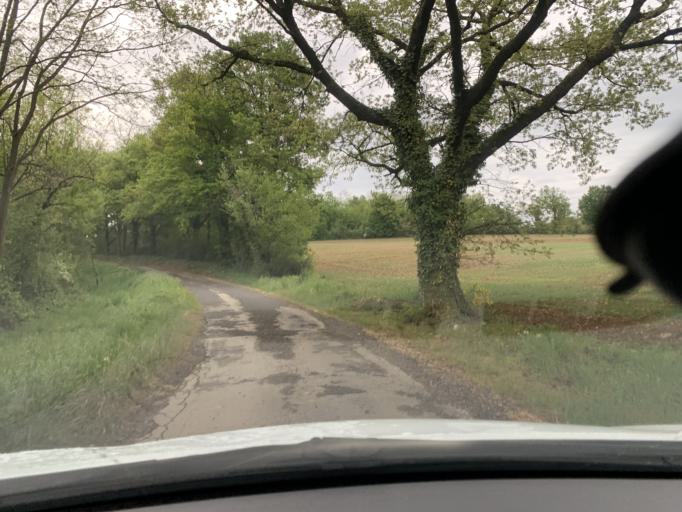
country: FR
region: Rhone-Alpes
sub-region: Departement du Rhone
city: Charnay
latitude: 45.9150
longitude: 4.6653
